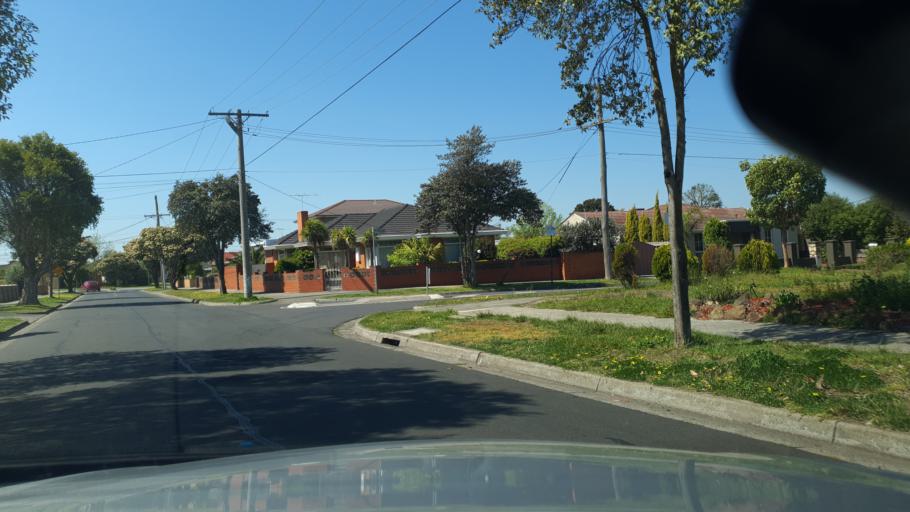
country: AU
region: Victoria
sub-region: Greater Dandenong
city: Springvale
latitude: -37.9318
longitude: 145.1709
